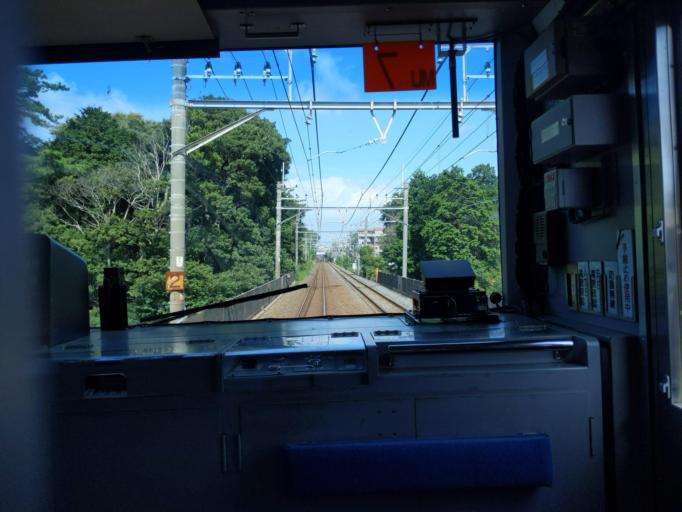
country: JP
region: Chiba
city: Funabashi
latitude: 35.7232
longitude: 139.9682
